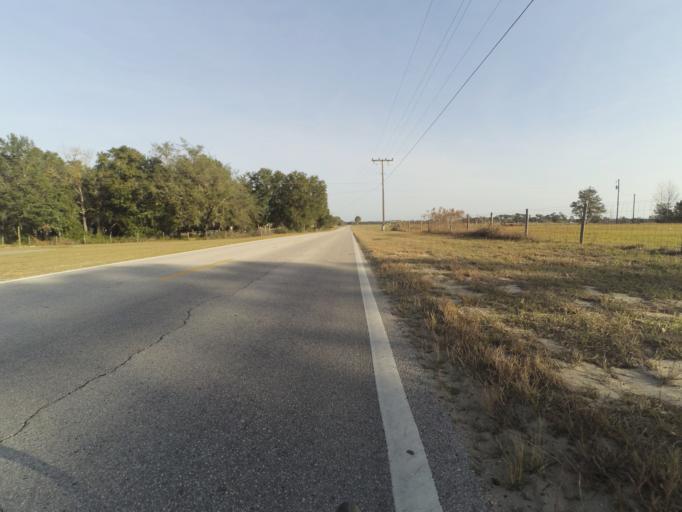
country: US
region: Florida
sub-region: Lake County
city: Umatilla
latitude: 28.9490
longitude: -81.6319
